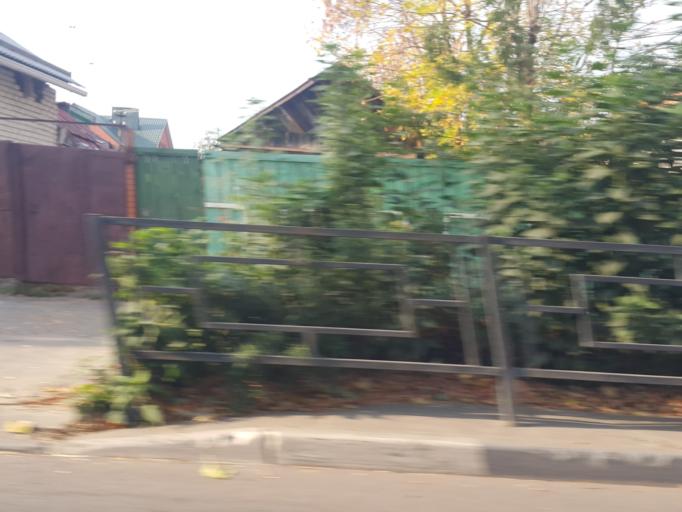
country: RU
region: Tambov
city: Tambov
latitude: 52.7096
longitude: 41.4598
